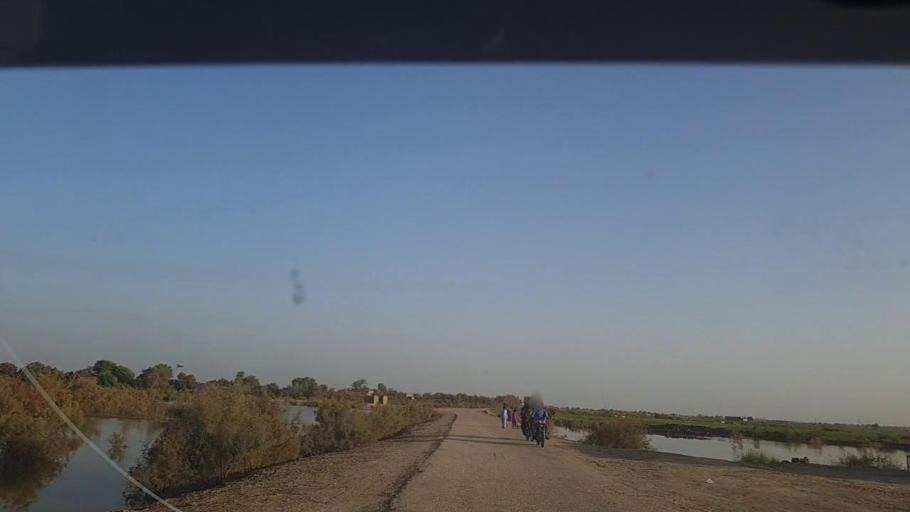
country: PK
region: Sindh
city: Thul
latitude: 28.1487
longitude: 68.8872
